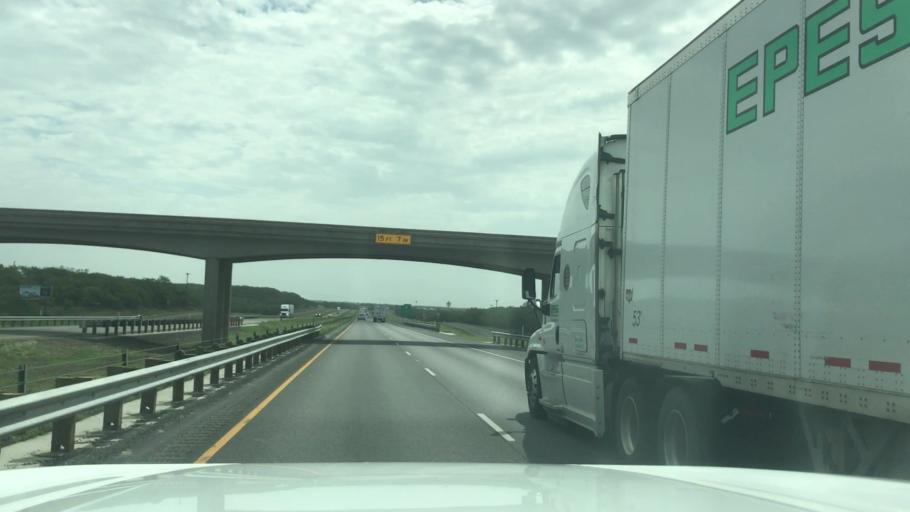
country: US
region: Texas
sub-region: Callahan County
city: Baird
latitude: 32.4032
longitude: -99.4076
